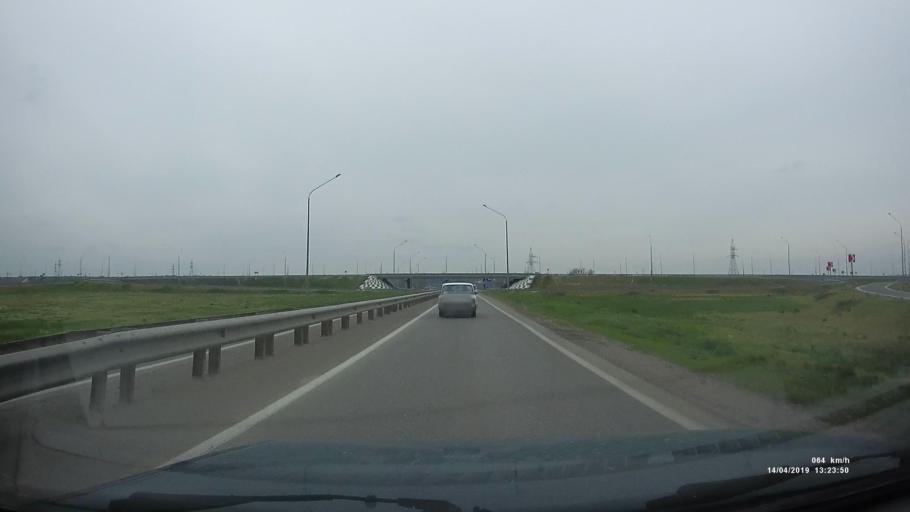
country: RU
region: Rostov
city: Kuleshovka
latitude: 47.0840
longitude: 39.4948
